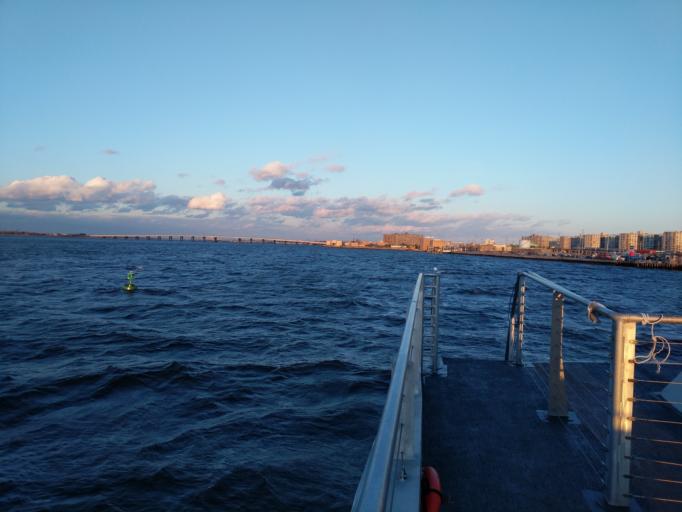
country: US
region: New York
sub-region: Kings County
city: East New York
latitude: 40.5837
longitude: -73.8382
